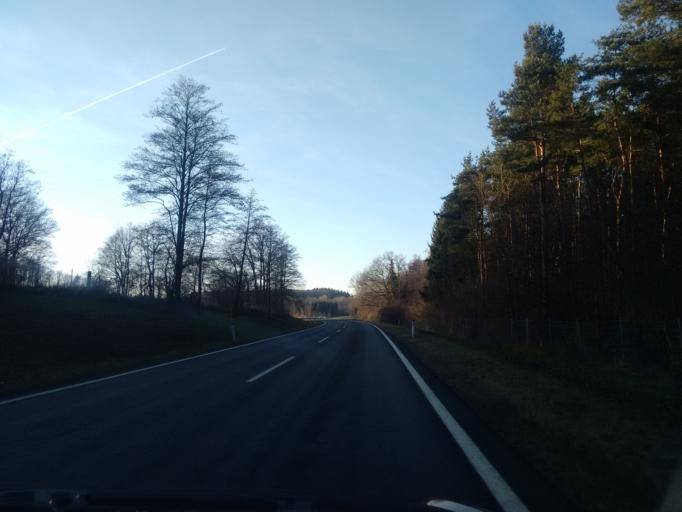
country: AT
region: Lower Austria
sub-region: Politischer Bezirk Sankt Polten
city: Neulengbach
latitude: 48.1832
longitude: 15.8697
